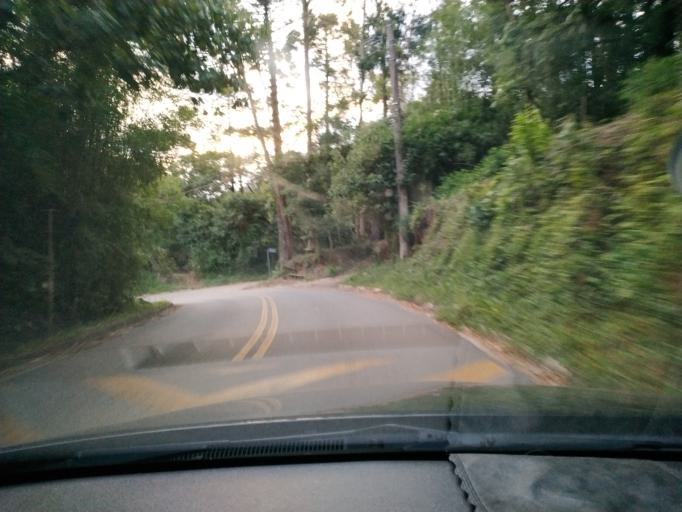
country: BR
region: Sao Paulo
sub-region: Campos Do Jordao
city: Campos do Jordao
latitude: -22.8072
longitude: -45.6448
